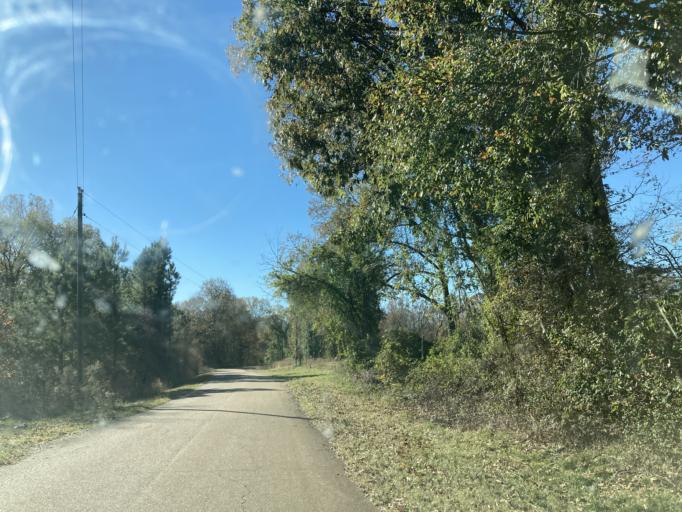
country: US
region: Mississippi
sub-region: Hinds County
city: Lynchburg
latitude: 32.5875
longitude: -90.5208
